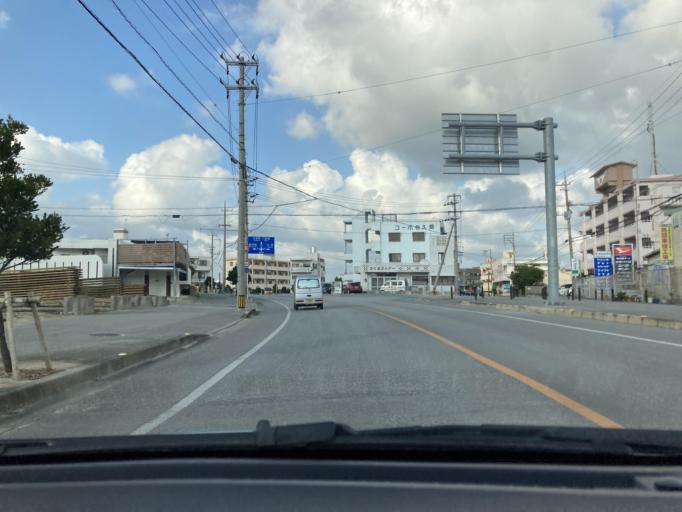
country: JP
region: Okinawa
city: Itoman
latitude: 26.1329
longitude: 127.6850
